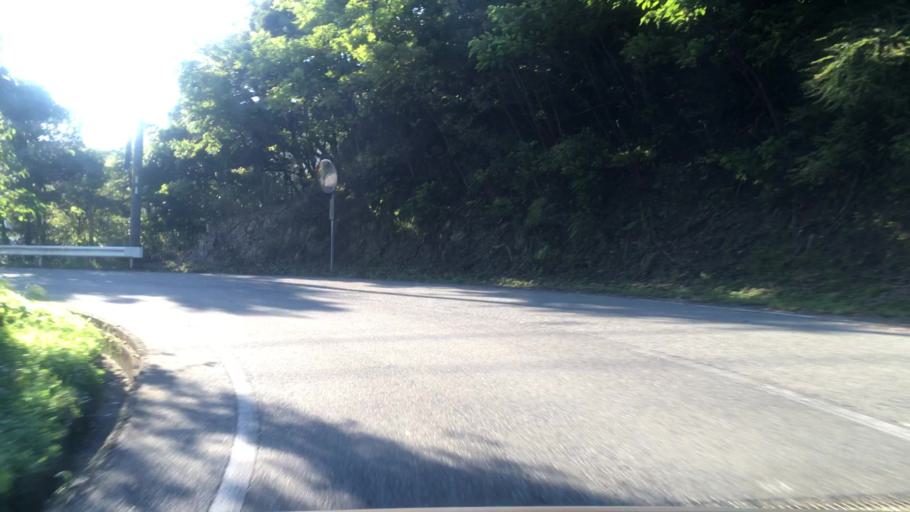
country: JP
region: Hyogo
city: Toyooka
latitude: 35.6060
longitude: 134.8063
